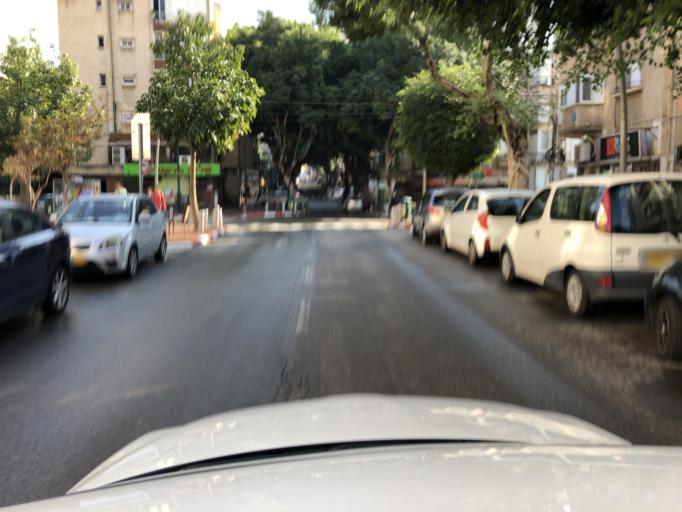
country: IL
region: Tel Aviv
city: Ramat Gan
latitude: 32.0922
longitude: 34.8179
